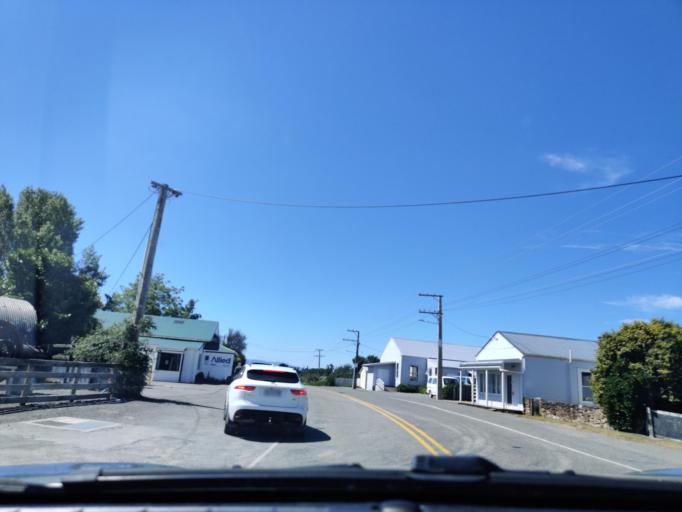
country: NZ
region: Wellington
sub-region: Upper Hutt City
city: Upper Hutt
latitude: -41.3527
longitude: 175.2055
